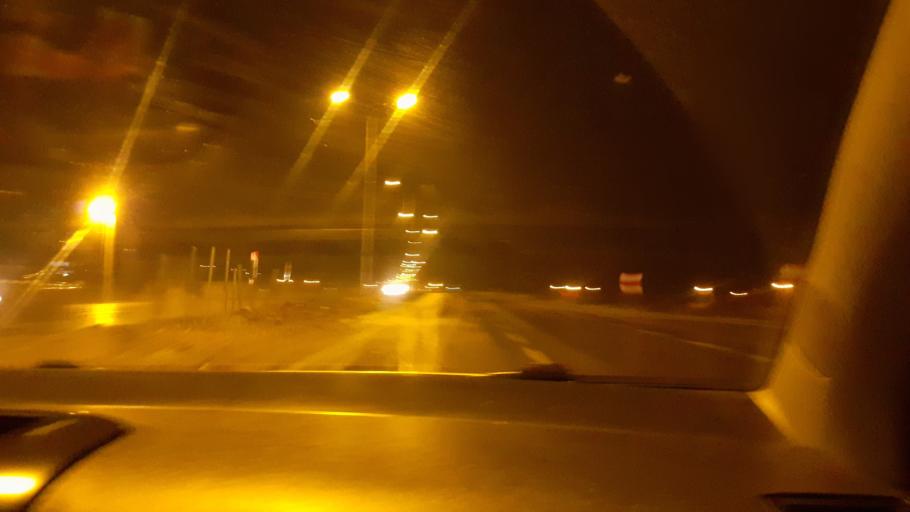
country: TR
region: Hatay
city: Aktepe
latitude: 36.7163
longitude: 36.5093
